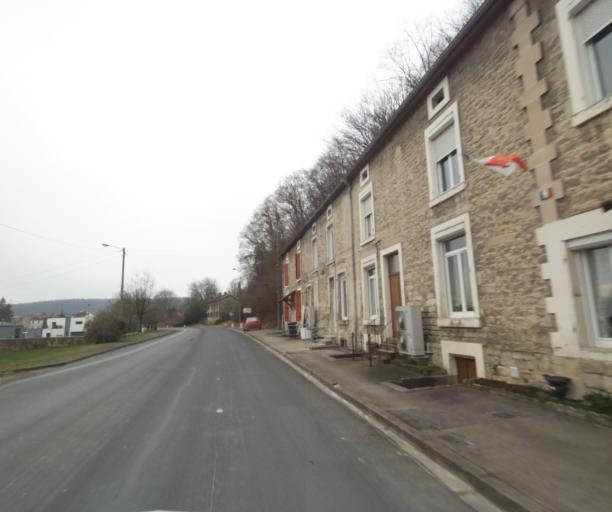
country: FR
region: Champagne-Ardenne
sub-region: Departement de la Haute-Marne
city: Chevillon
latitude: 48.5326
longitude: 5.0971
